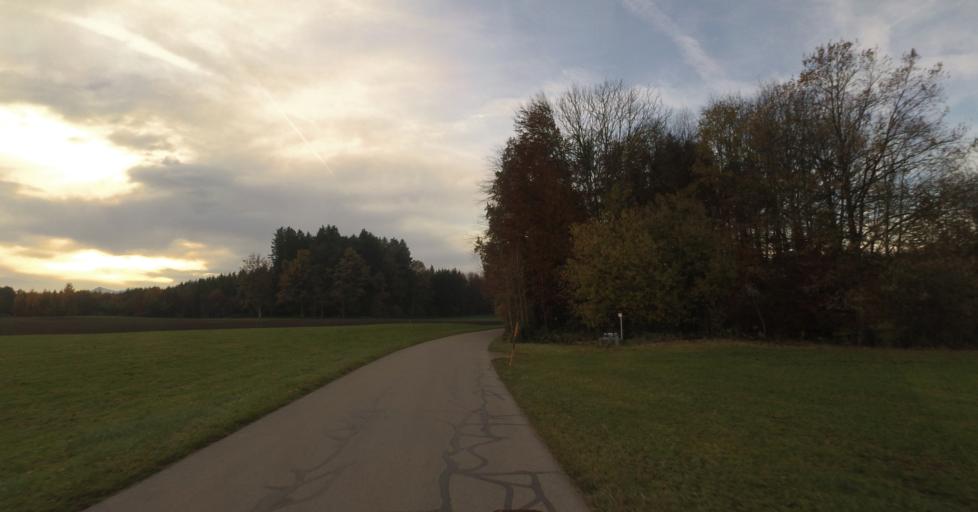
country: DE
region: Bavaria
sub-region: Upper Bavaria
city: Nussdorf
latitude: 47.8899
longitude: 12.6060
